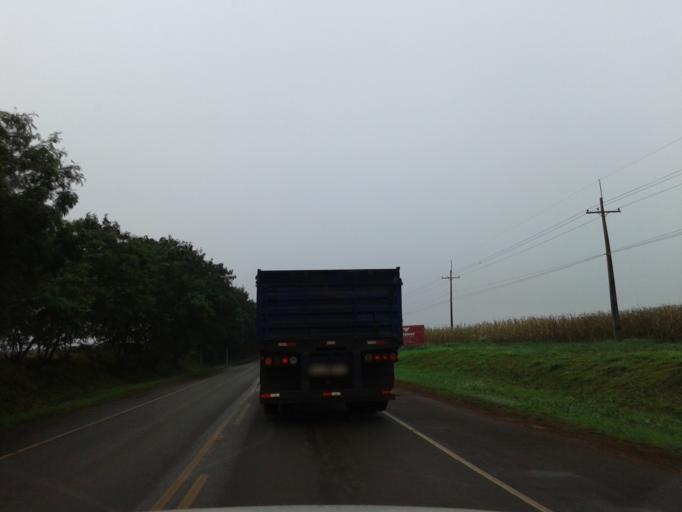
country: PY
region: Alto Parana
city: Naranjal
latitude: -25.9458
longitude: -55.1216
